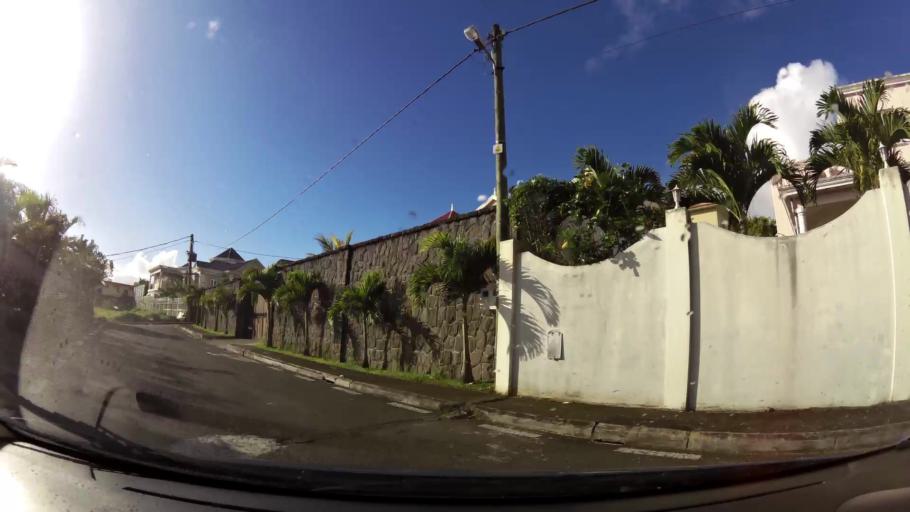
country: MU
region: Plaines Wilhems
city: Vacoas
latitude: -20.3087
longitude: 57.4959
